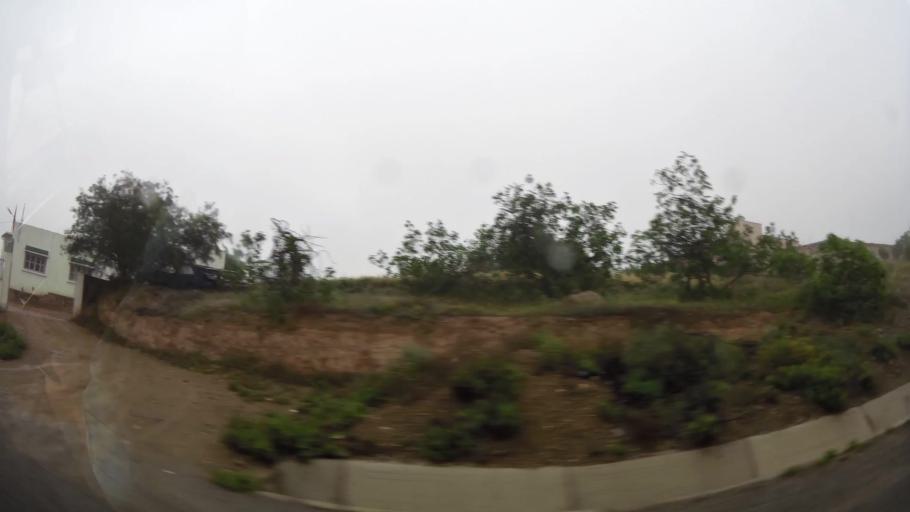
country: MA
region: Oriental
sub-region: Nador
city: Boudinar
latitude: 35.1273
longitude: -3.5804
